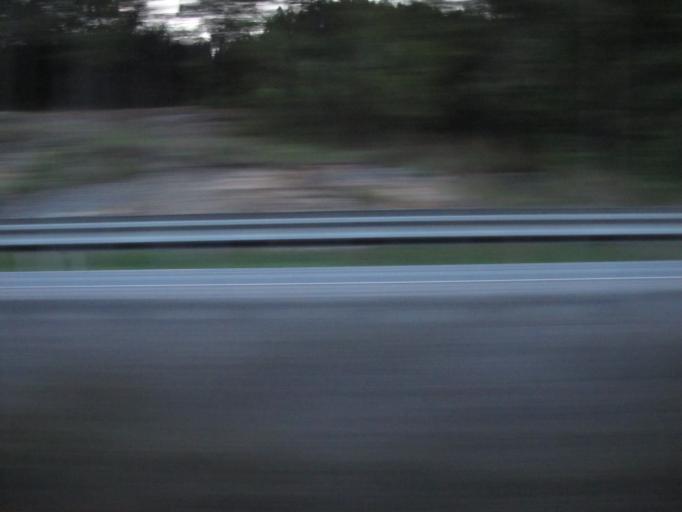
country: NO
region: Oppland
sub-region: Ringebu
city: Ringebu
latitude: 61.5422
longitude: 10.0843
